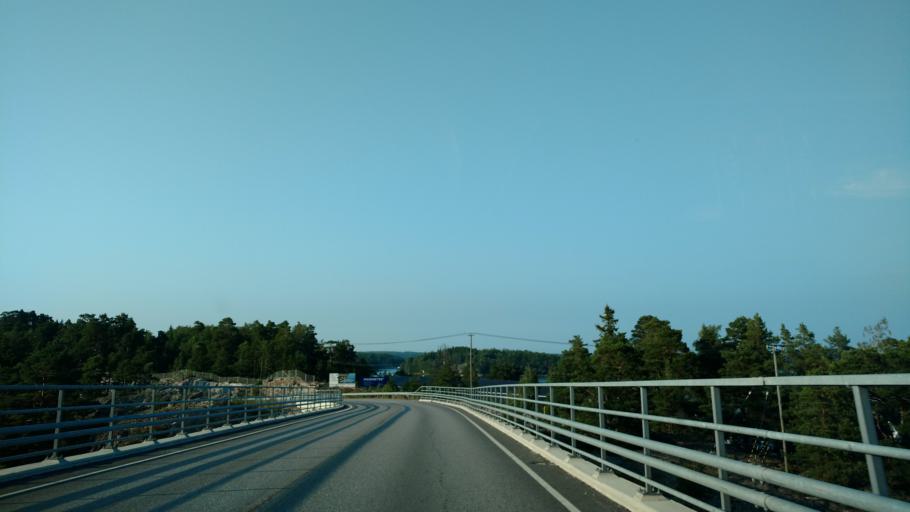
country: FI
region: Varsinais-Suomi
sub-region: Aboland-Turunmaa
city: Dragsfjaerd
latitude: 59.9859
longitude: 22.4542
